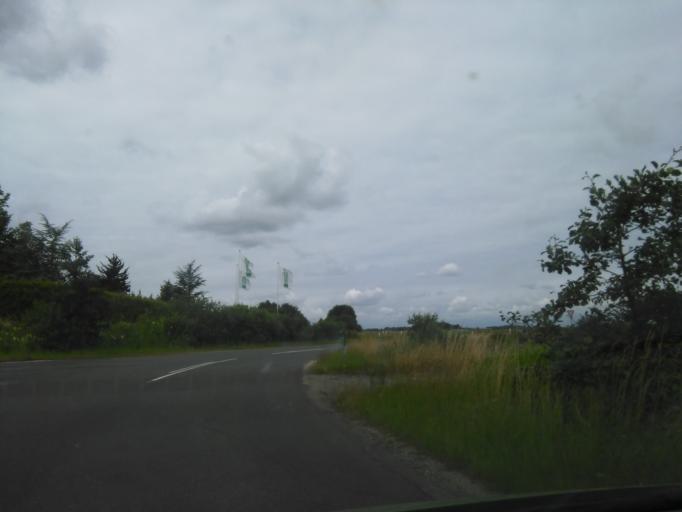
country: DK
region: Central Jutland
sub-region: Arhus Kommune
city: Solbjerg
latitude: 56.0304
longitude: 10.0641
